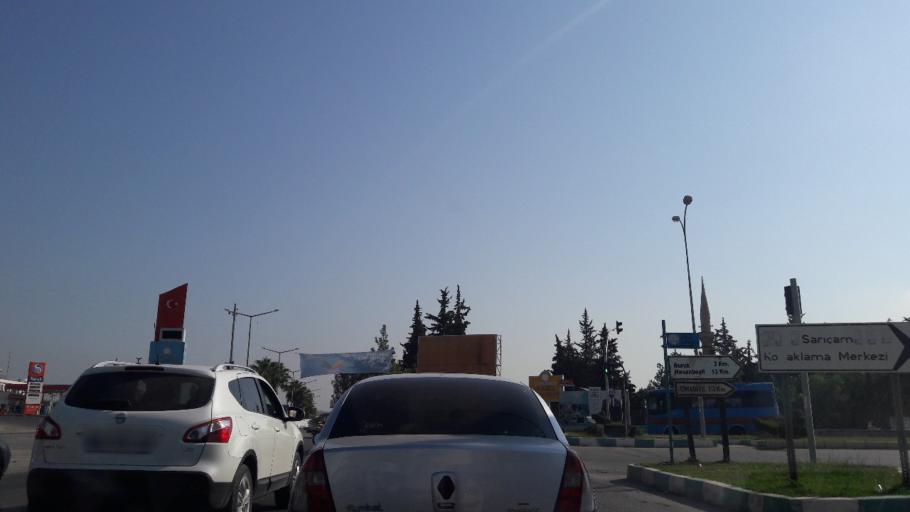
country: TR
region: Adana
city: Yuregir
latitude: 37.0415
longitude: 35.4297
